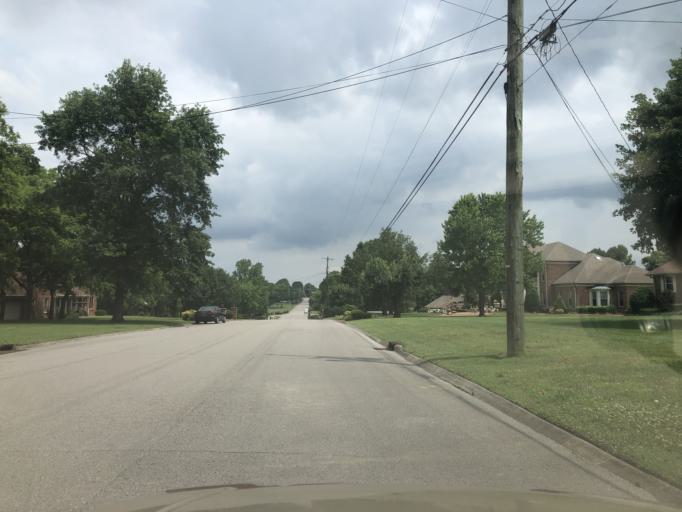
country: US
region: Tennessee
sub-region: Davidson County
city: Lakewood
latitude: 36.2362
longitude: -86.6103
